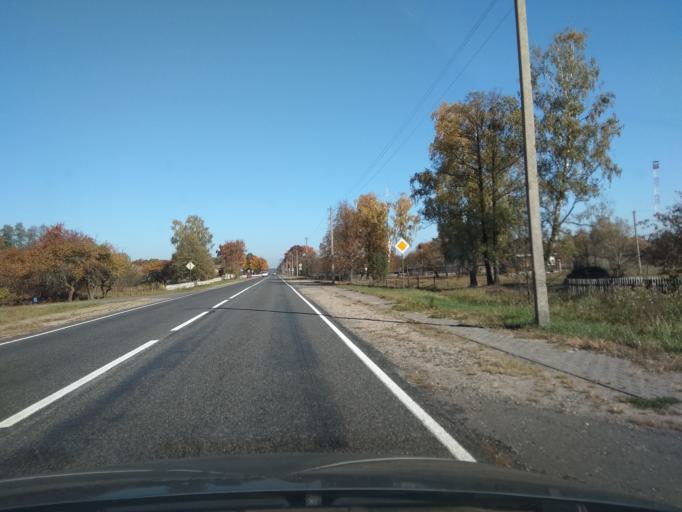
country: BY
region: Brest
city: Malaryta
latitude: 51.9838
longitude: 24.2046
